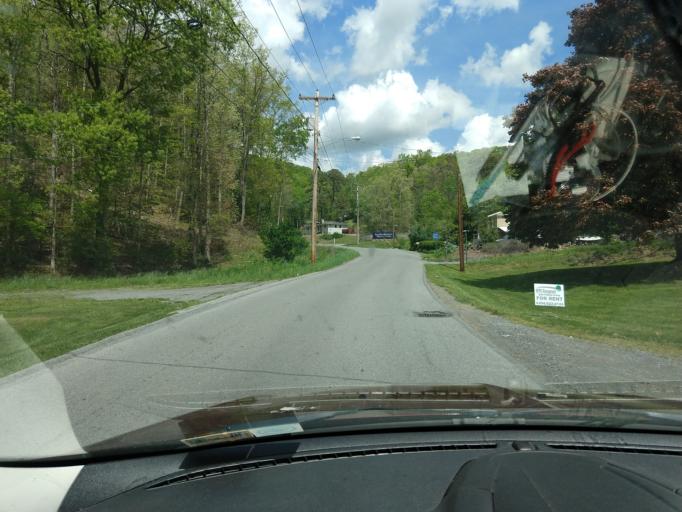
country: US
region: West Virginia
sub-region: Mercer County
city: Bluefield
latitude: 37.2525
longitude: -81.2391
